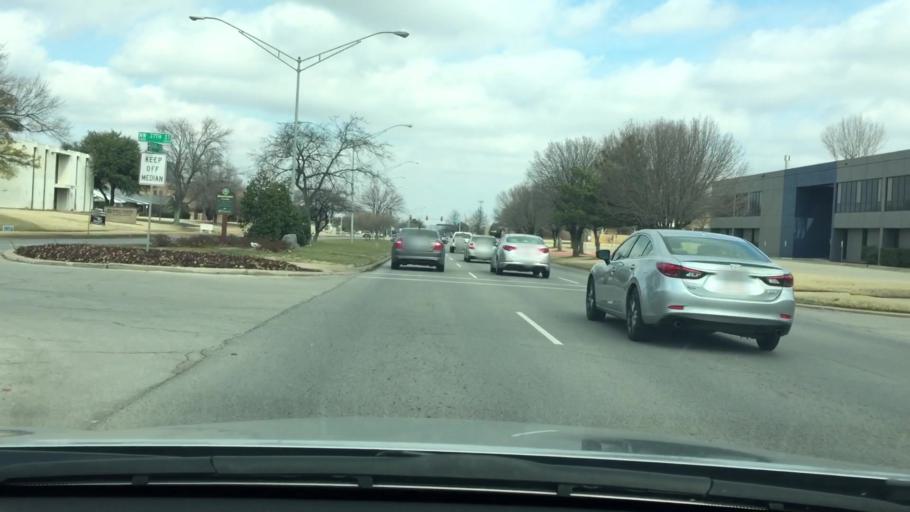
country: US
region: Oklahoma
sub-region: Oklahoma County
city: Nichols Hills
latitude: 35.5089
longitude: -97.5343
